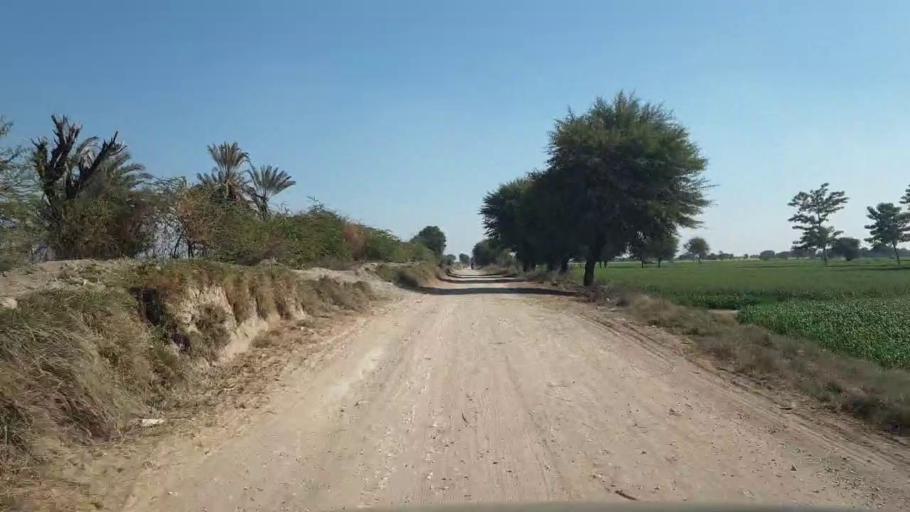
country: PK
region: Sindh
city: Shahpur Chakar
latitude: 26.1451
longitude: 68.6483
